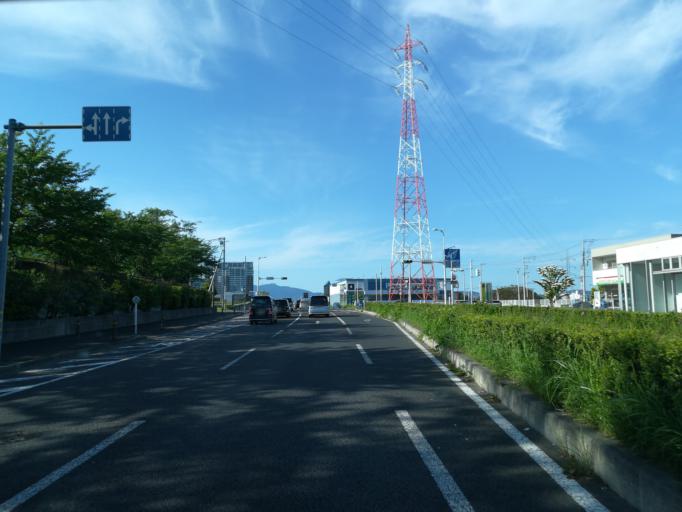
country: JP
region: Ibaraki
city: Naka
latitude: 36.0745
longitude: 140.0852
